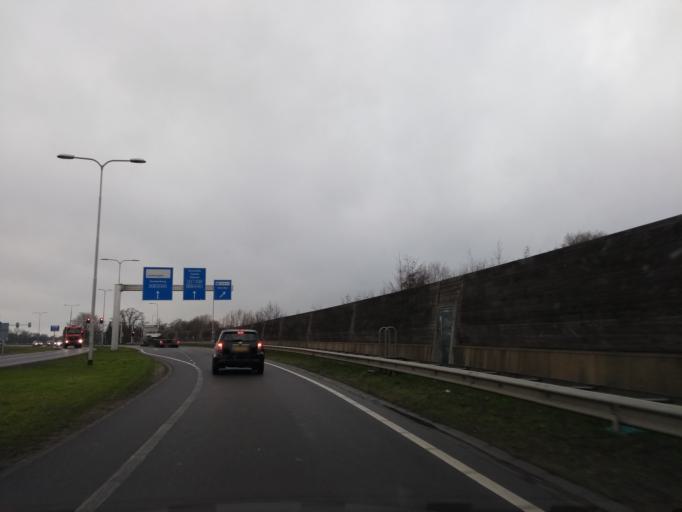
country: NL
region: Overijssel
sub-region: Gemeente Wierden
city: Wierden
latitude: 52.3550
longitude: 6.6114
